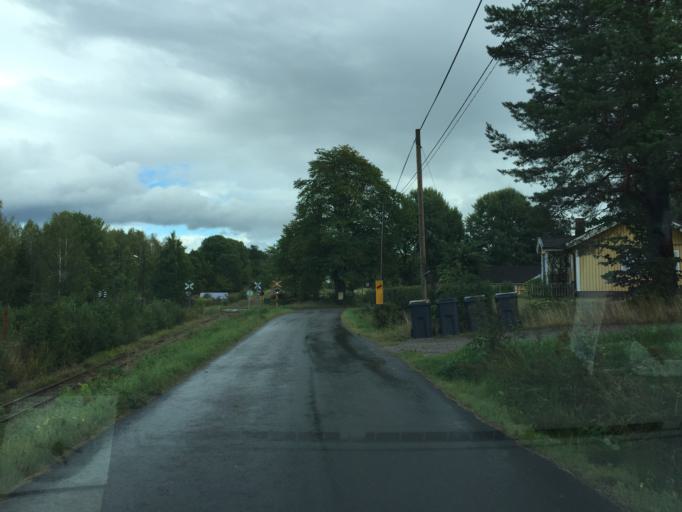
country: SE
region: Kalmar
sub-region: Vasterviks Kommun
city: Ankarsrum
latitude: 57.7373
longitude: 16.4160
